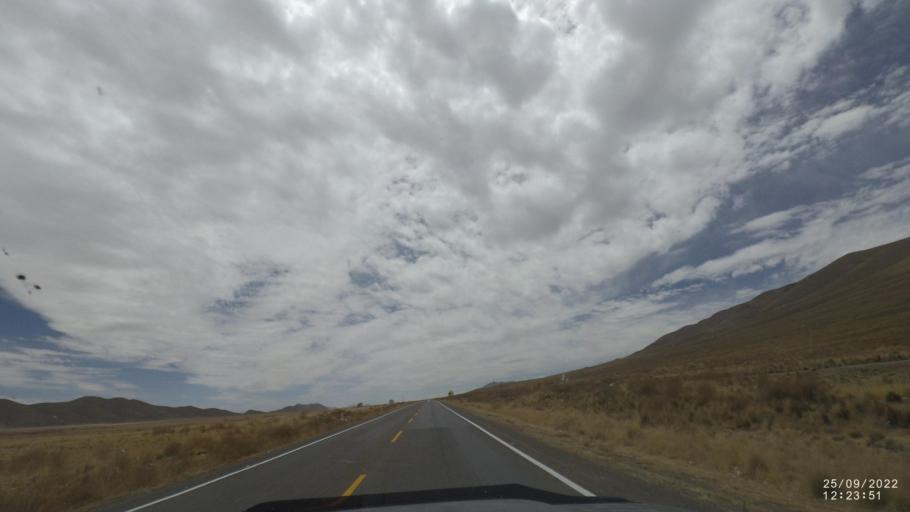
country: BO
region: Oruro
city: Poopo
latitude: -18.3647
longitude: -66.9818
